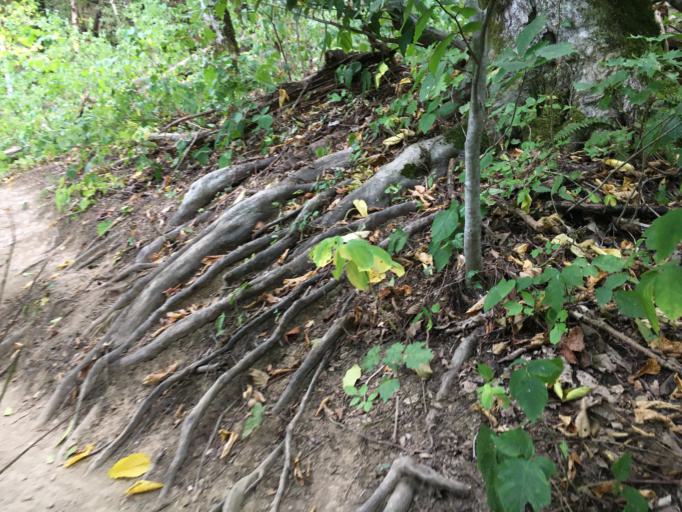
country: RU
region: Krasnodarskiy
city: Tuapse
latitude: 44.2512
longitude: 39.2303
